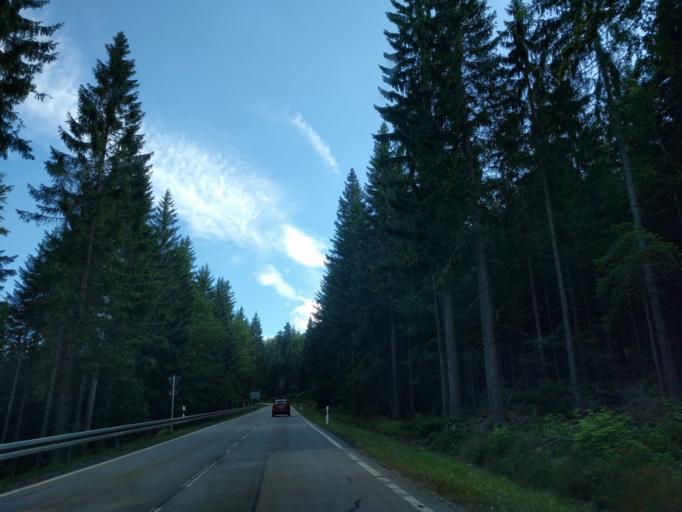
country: DE
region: Bavaria
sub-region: Lower Bavaria
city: Bayerisch Eisenstein
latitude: 49.0966
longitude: 13.1614
